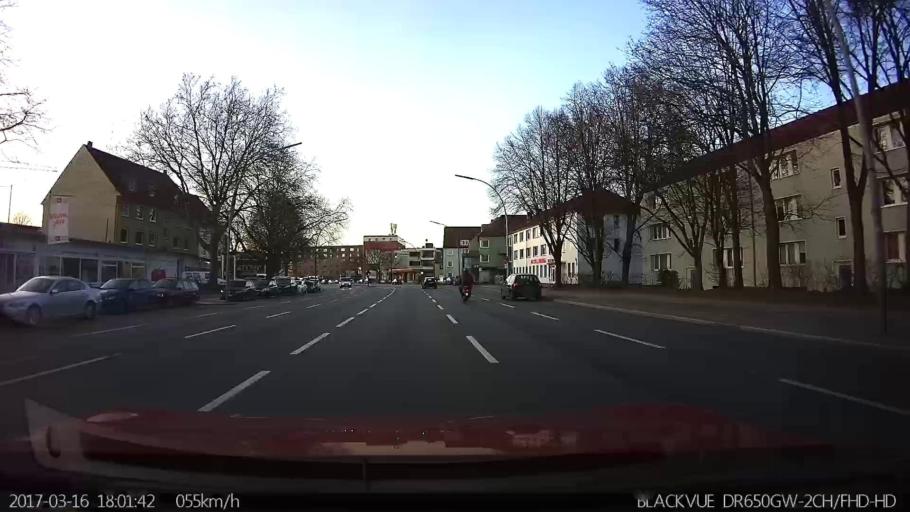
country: DE
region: Hamburg
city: Stellingen
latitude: 53.5905
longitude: 9.9306
